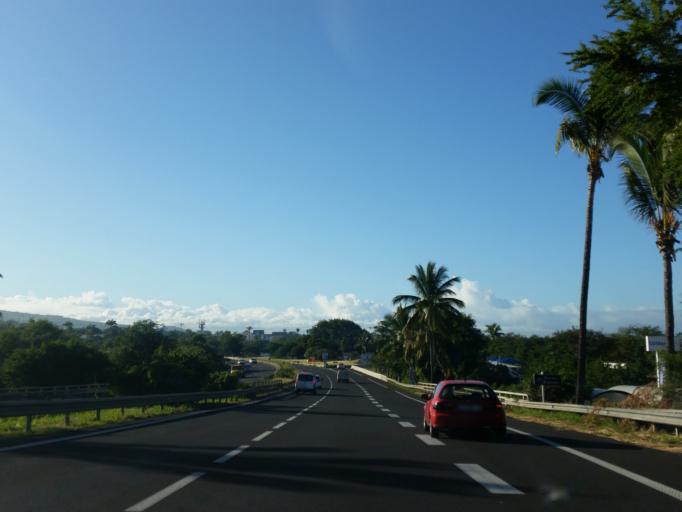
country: RE
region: Reunion
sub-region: Reunion
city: Saint-Pierre
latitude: -21.3324
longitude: 55.4586
